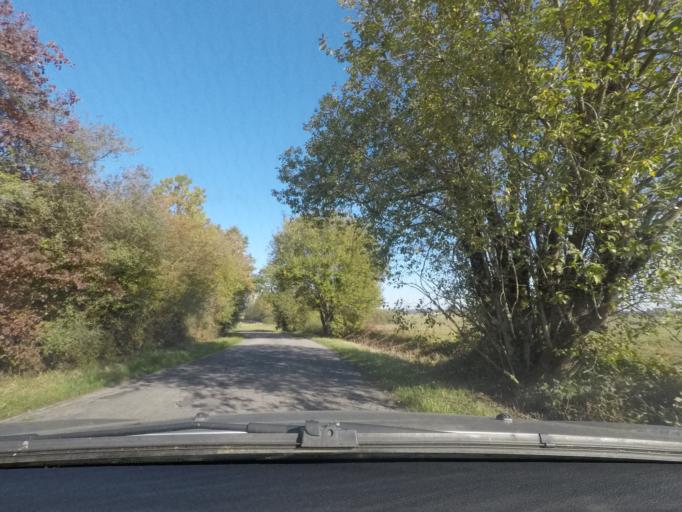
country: BE
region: Wallonia
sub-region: Province du Luxembourg
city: Etalle
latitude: 49.7050
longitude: 5.5680
